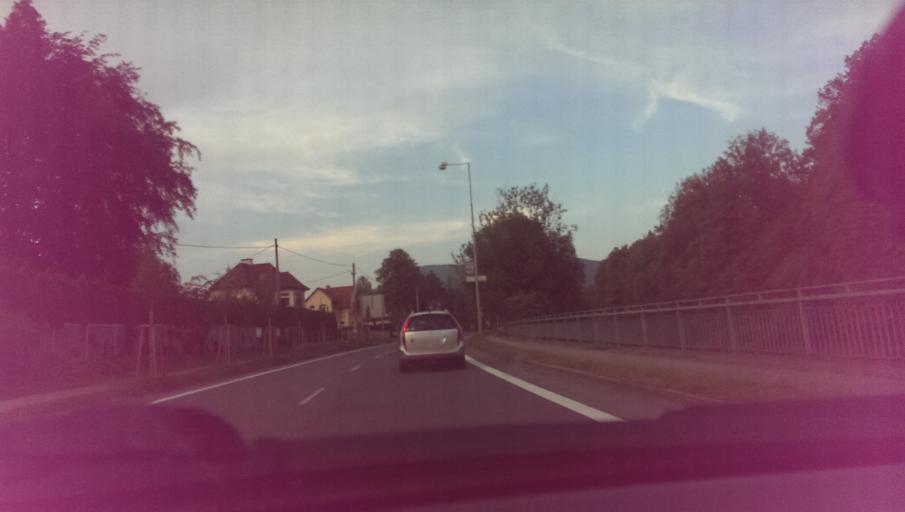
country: CZ
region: Zlin
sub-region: Okres Vsetin
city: Roznov pod Radhostem
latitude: 49.4614
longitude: 18.1402
